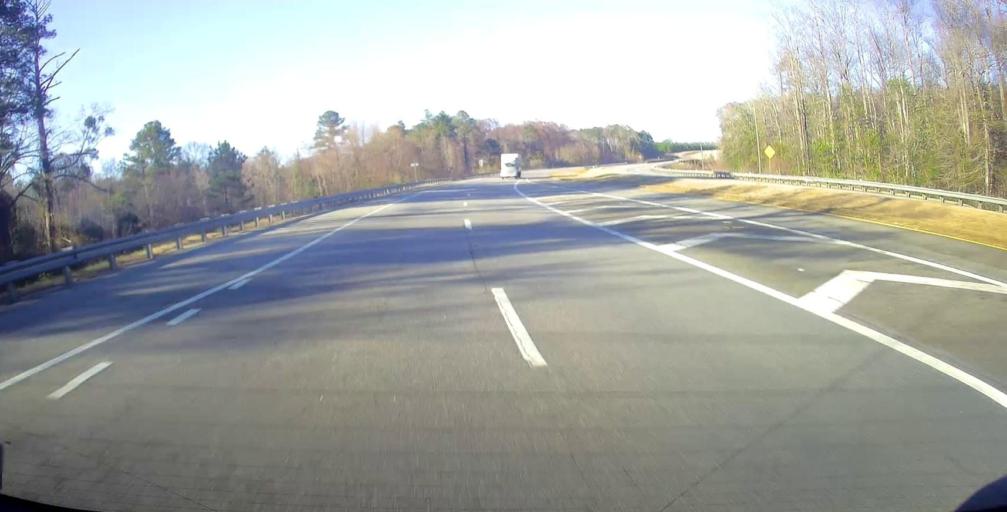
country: US
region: Georgia
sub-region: Sumter County
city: Americus
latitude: 31.9255
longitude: -84.2659
